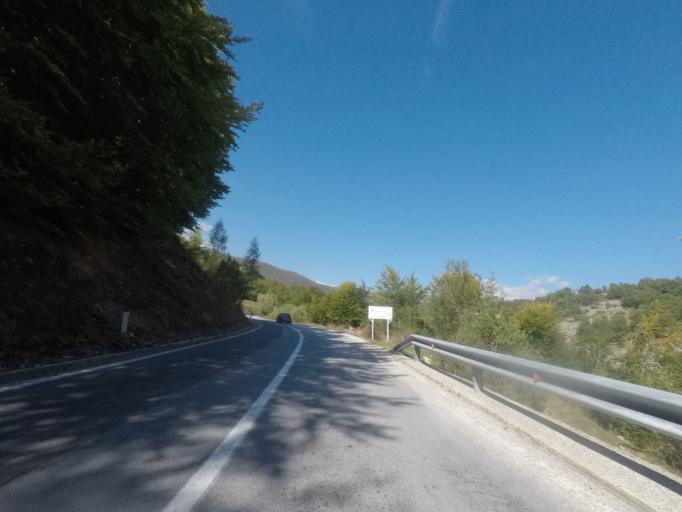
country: ME
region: Opstina Pluzine
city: Pluzine
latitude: 43.1151
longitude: 18.8208
